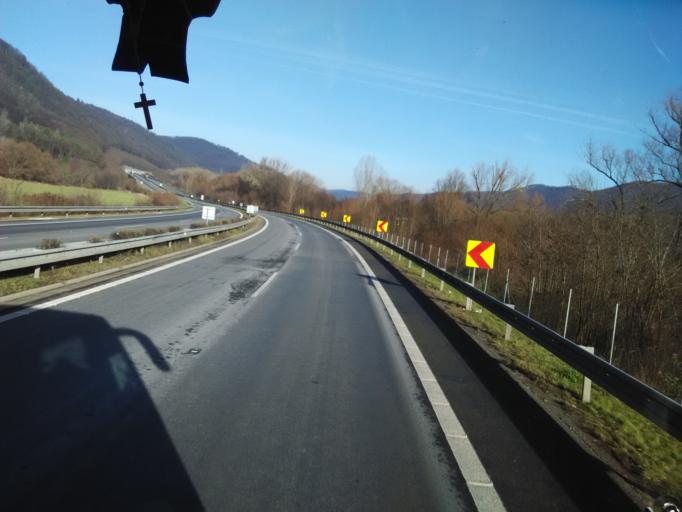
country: SK
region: Banskobystricky
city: Nova Bana
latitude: 48.4195
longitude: 18.6649
